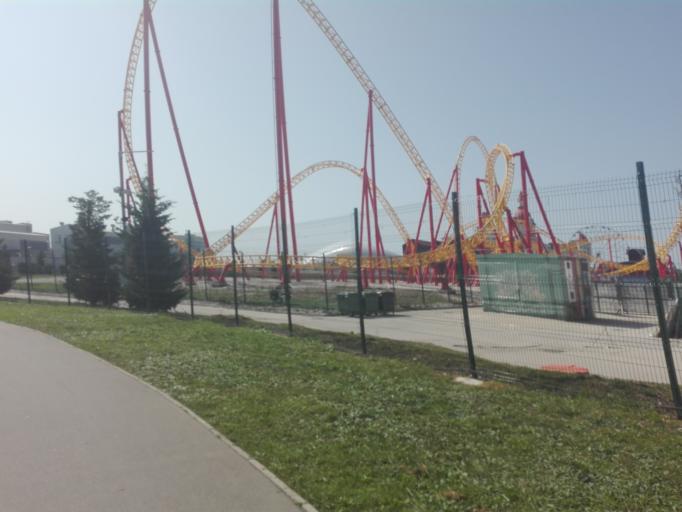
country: RU
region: Krasnodarskiy
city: Adler
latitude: 43.4028
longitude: 39.9692
